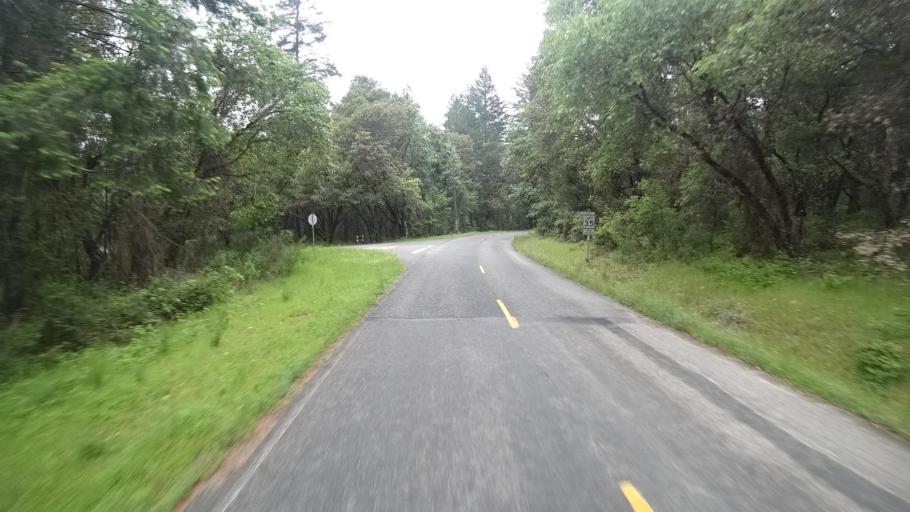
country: US
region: California
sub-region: Humboldt County
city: Willow Creek
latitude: 41.0413
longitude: -123.6590
